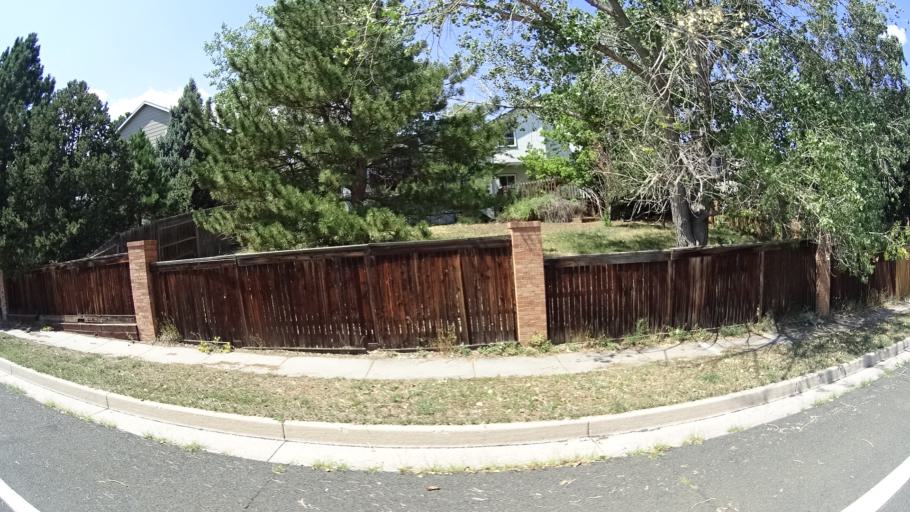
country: US
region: Colorado
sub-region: El Paso County
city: Air Force Academy
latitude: 38.9223
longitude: -104.8675
